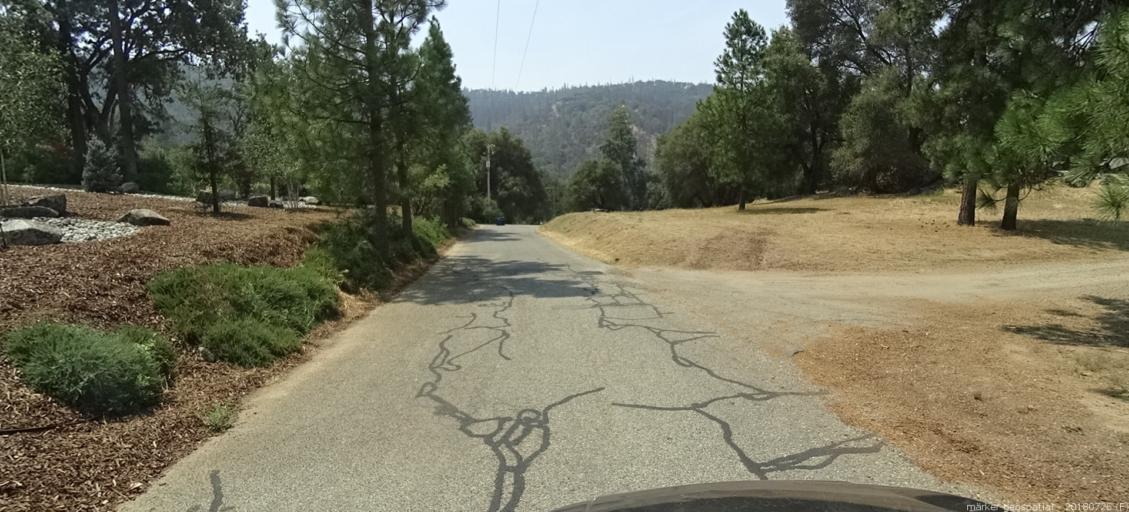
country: US
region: California
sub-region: Madera County
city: Oakhurst
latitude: 37.2846
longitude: -119.6465
